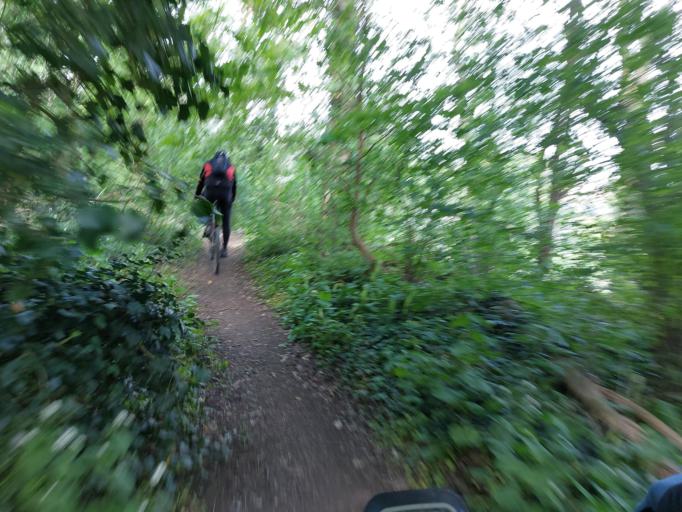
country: BE
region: Wallonia
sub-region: Province du Hainaut
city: Frameries
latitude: 50.4011
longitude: 3.9018
